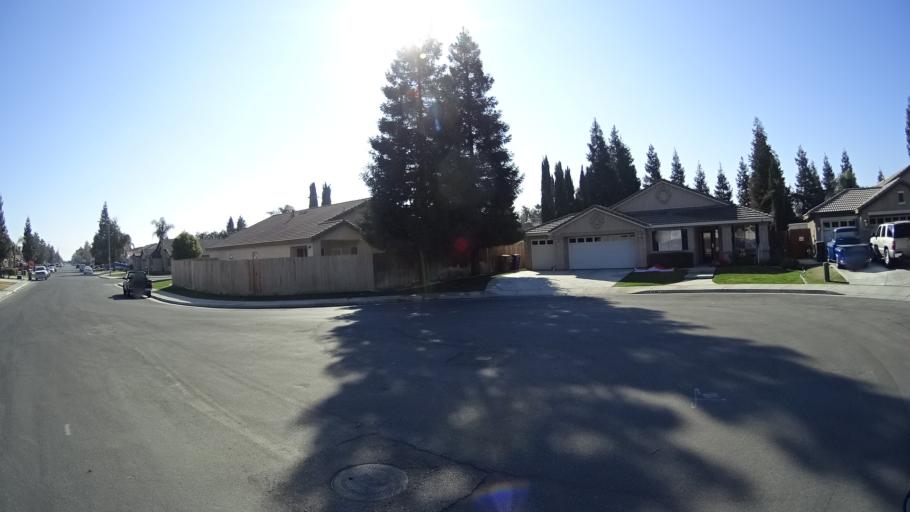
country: US
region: California
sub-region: Kern County
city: Greenacres
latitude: 35.3142
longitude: -119.1169
